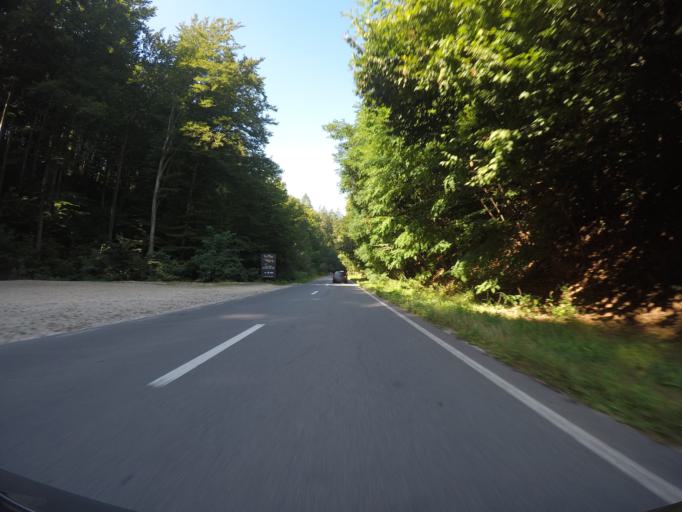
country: RO
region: Brasov
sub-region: Comuna Cristian
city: Cristian
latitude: 45.5853
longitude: 25.4934
